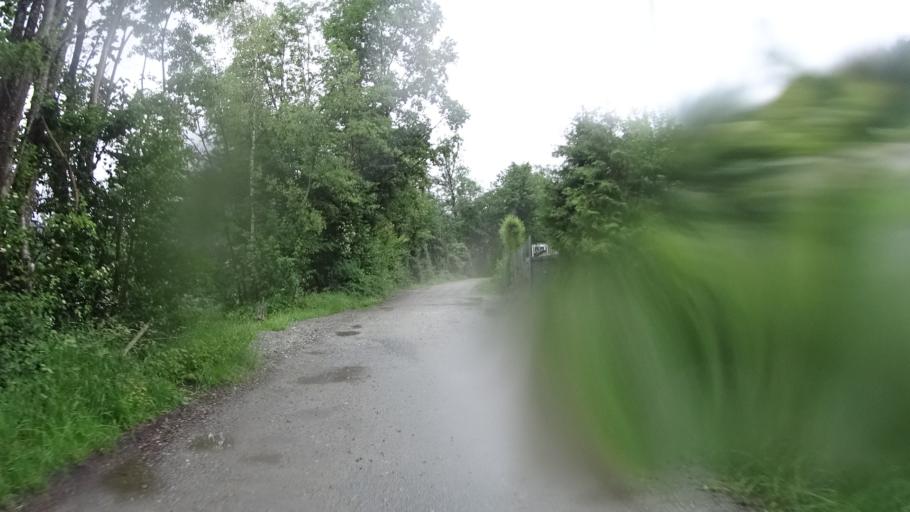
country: AT
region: Upper Austria
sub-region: Politischer Bezirk Scharding
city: Scharding
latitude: 48.5106
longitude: 13.4542
